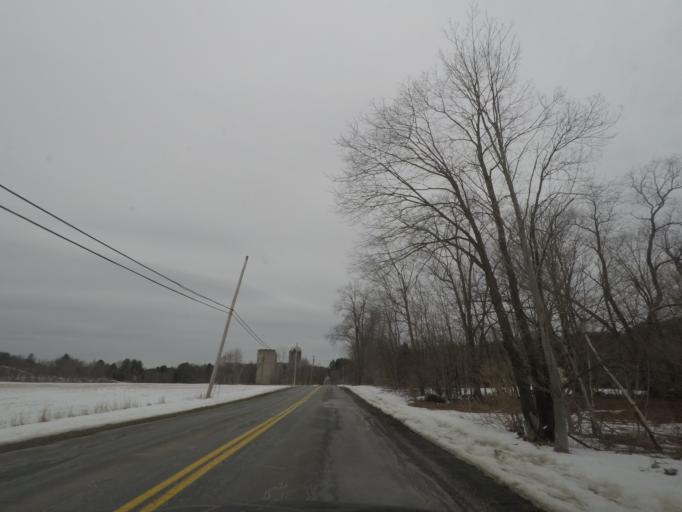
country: US
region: Massachusetts
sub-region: Berkshire County
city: Lanesborough
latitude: 42.5848
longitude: -73.3735
